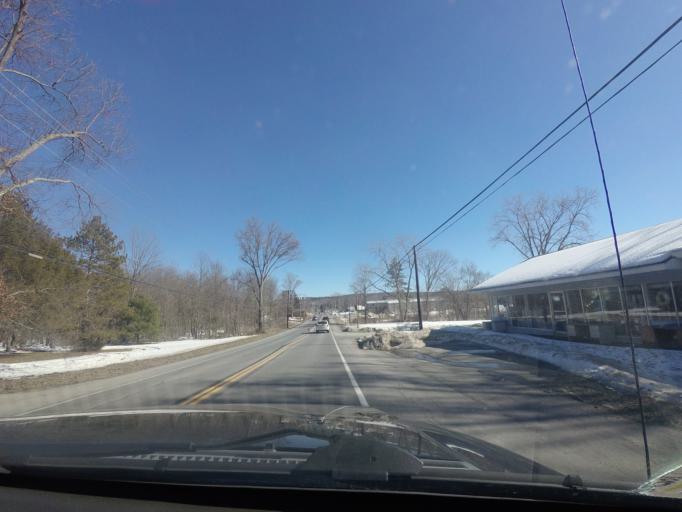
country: US
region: New York
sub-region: Rensselaer County
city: Nassau
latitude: 42.5185
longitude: -73.6228
